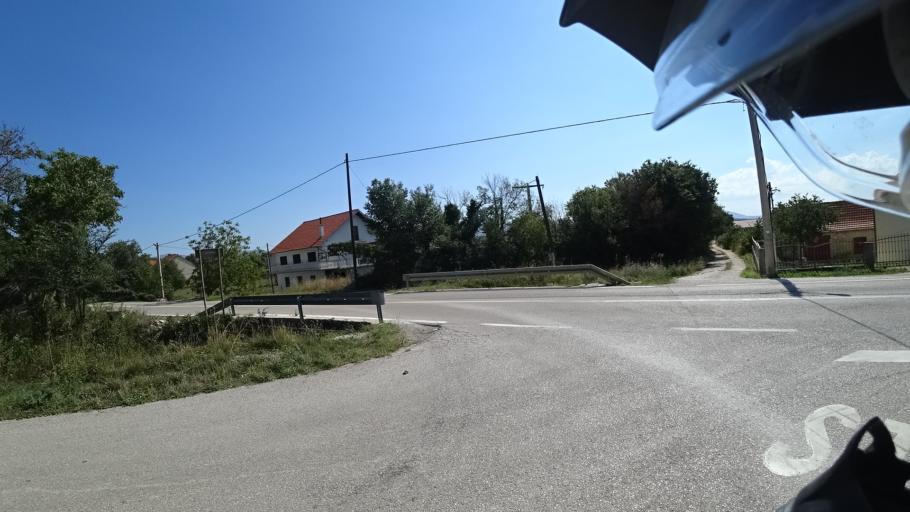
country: HR
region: Sibensko-Kniniska
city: Drnis
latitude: 43.8773
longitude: 16.2010
